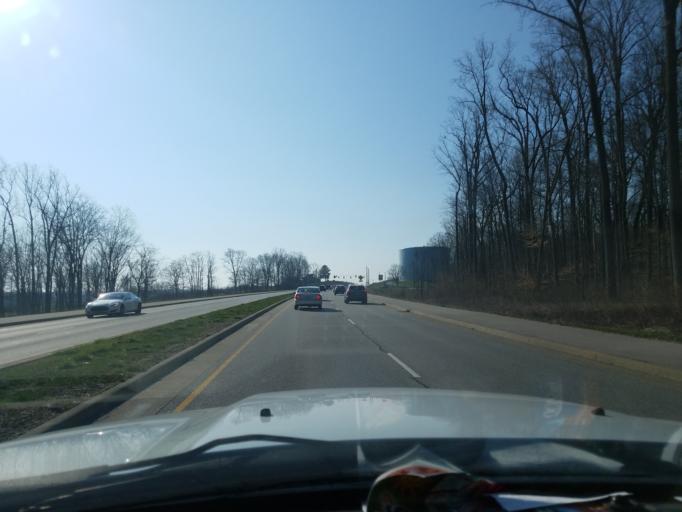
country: US
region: Indiana
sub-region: Monroe County
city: Bloomington
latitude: 39.1816
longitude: -86.5094
